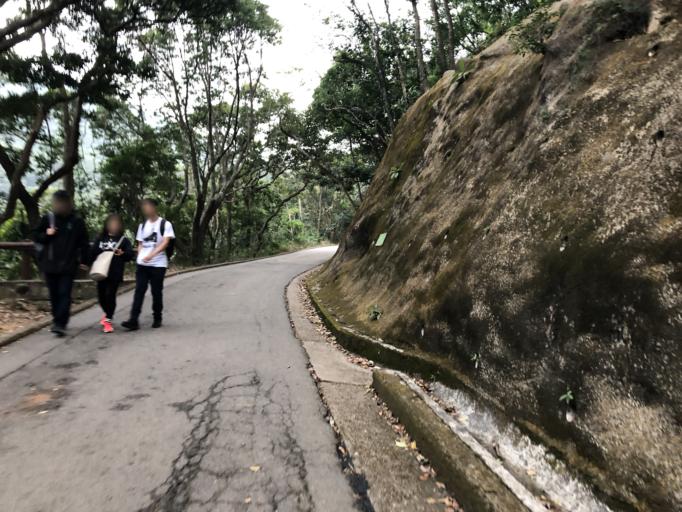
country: HK
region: Wanchai
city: Wan Chai
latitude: 22.2684
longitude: 114.2127
